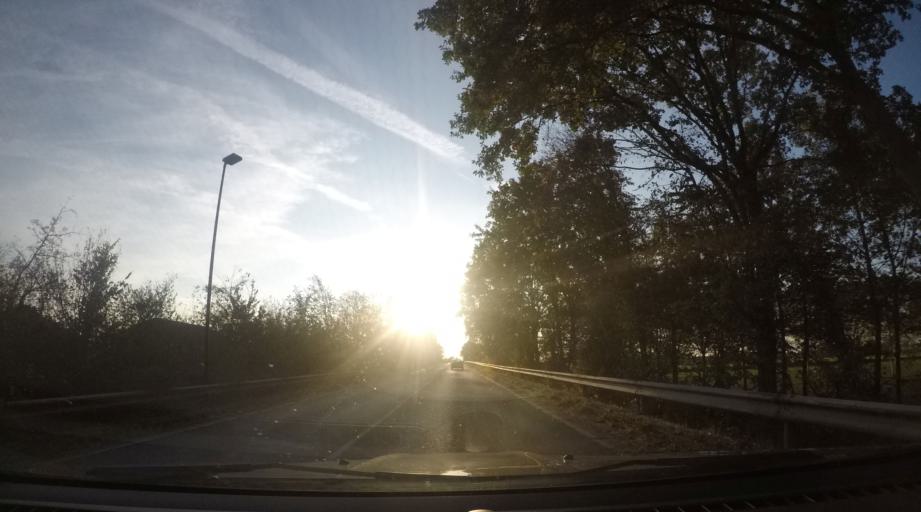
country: DE
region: North Rhine-Westphalia
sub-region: Regierungsbezirk Dusseldorf
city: Hamminkeln
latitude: 51.7746
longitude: 6.6105
